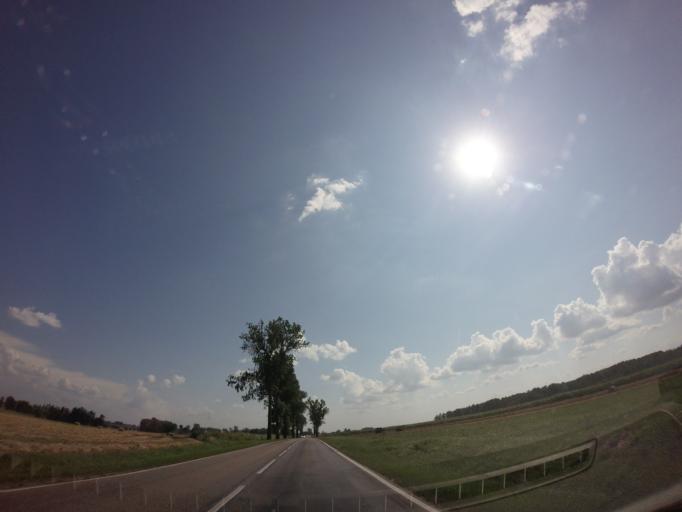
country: PL
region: Podlasie
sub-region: Powiat zambrowski
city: Zambrow
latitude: 52.8951
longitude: 22.2518
